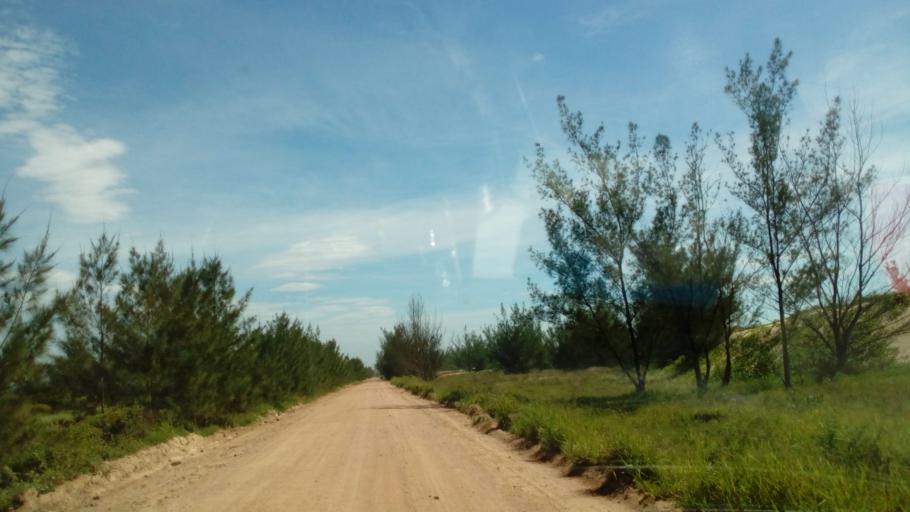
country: BR
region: Santa Catarina
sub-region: Laguna
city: Laguna
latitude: -28.4544
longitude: -48.7652
